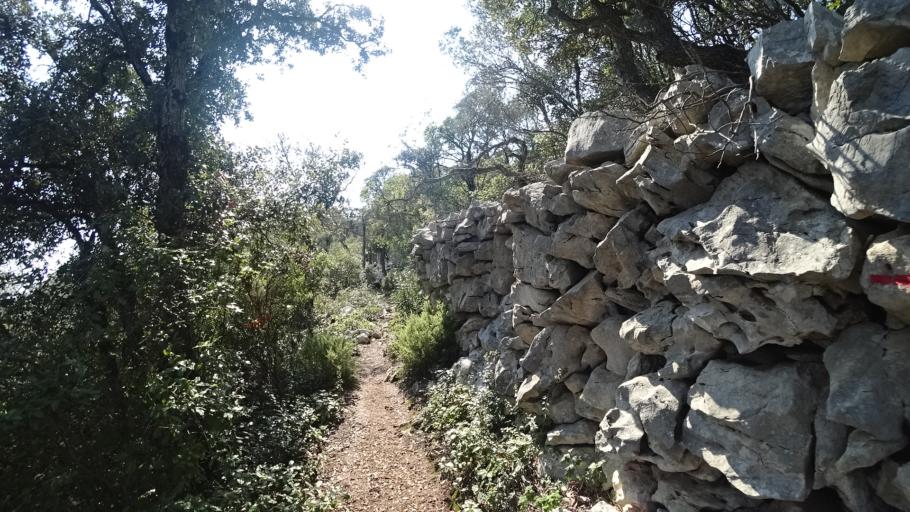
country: HR
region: Primorsko-Goranska
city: Mali Losinj
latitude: 44.4919
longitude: 14.5306
